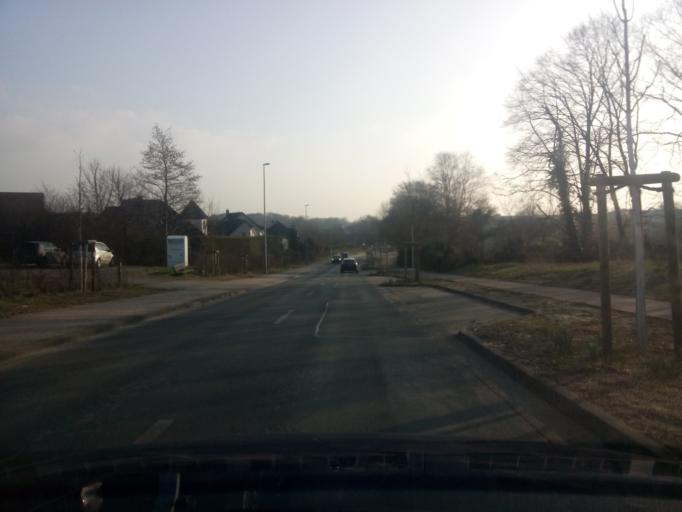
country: DE
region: Lower Saxony
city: Osterholz-Scharmbeck
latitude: 53.2312
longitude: 8.7992
